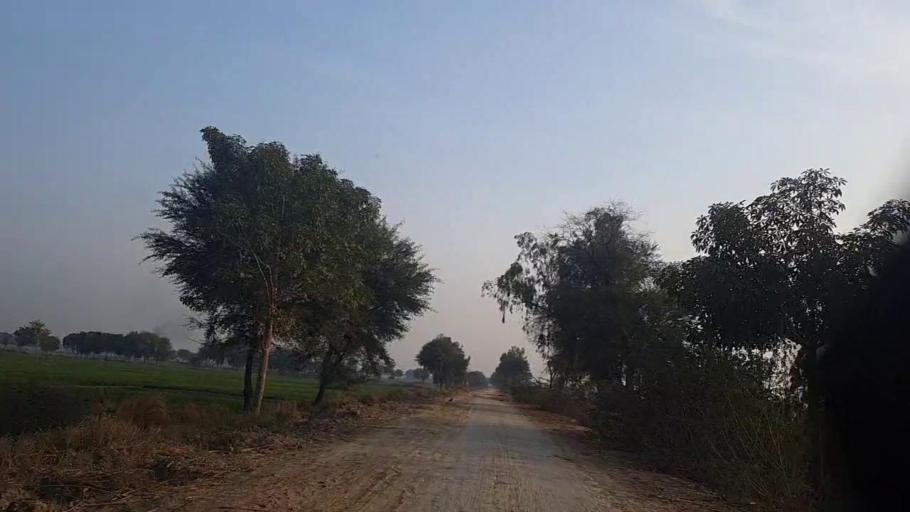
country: PK
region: Sindh
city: Sakrand
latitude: 26.1259
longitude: 68.2299
